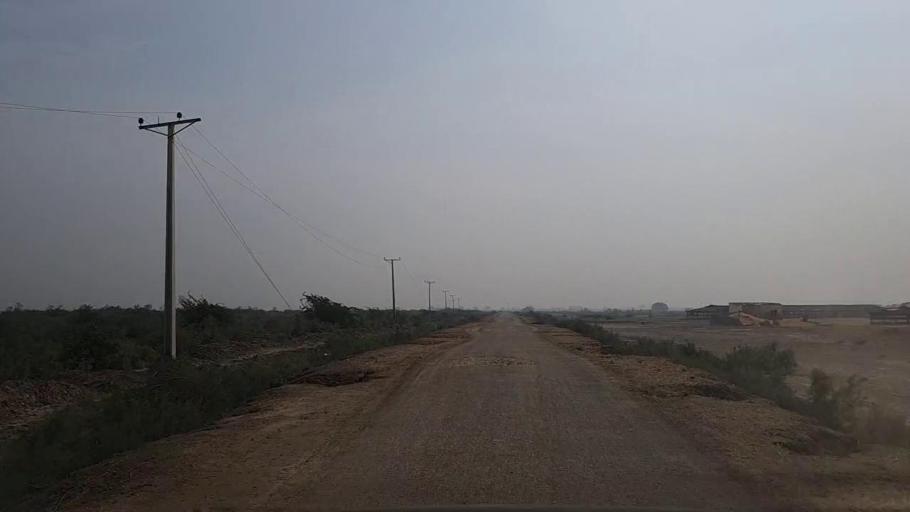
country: PK
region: Sindh
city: Mirpur Sakro
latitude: 24.3898
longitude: 67.7519
